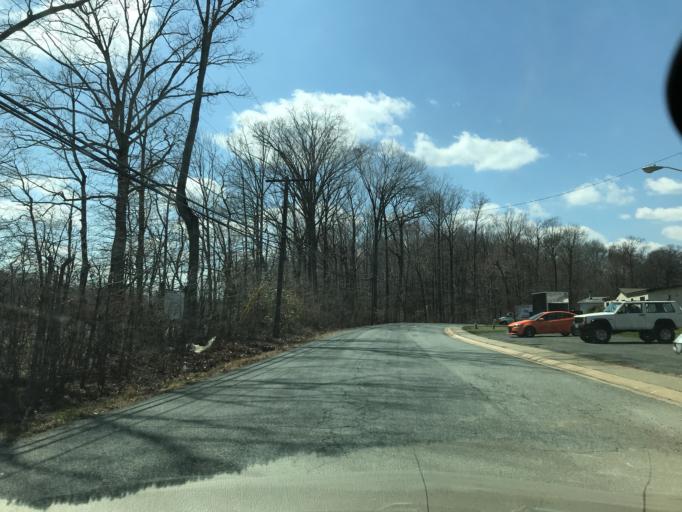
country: US
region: Maryland
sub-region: Harford County
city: Perryman
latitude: 39.4480
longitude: -76.2248
